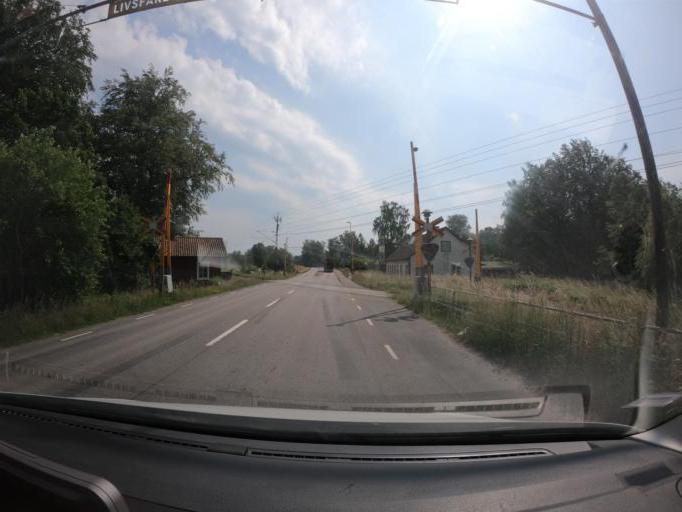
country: SE
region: Skane
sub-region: Hassleholms Kommun
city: Bjarnum
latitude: 56.3506
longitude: 13.6618
